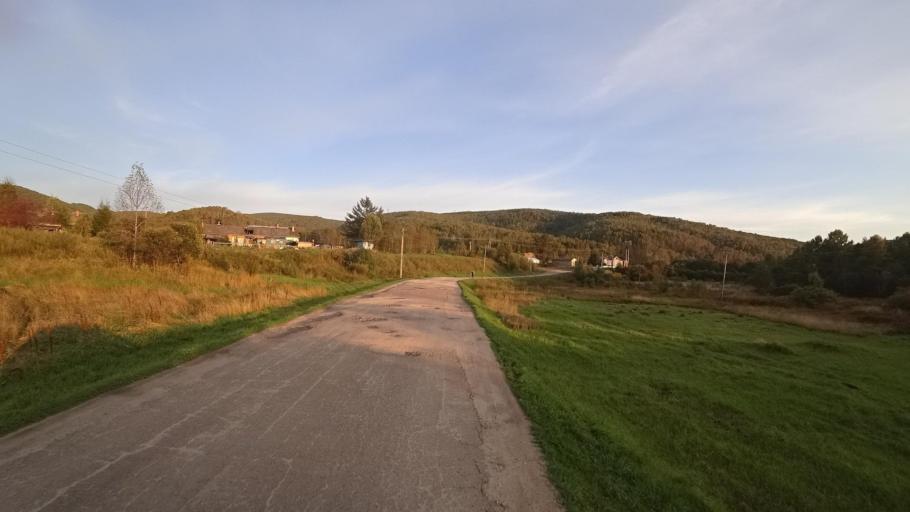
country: RU
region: Jewish Autonomous Oblast
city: Kul'dur
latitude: 49.1982
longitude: 131.6329
